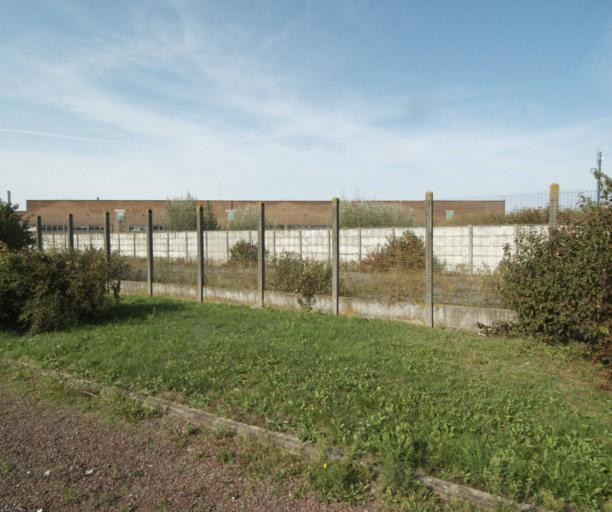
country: FR
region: Nord-Pas-de-Calais
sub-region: Departement du Nord
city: Wambrechies
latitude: 50.6776
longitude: 3.0546
